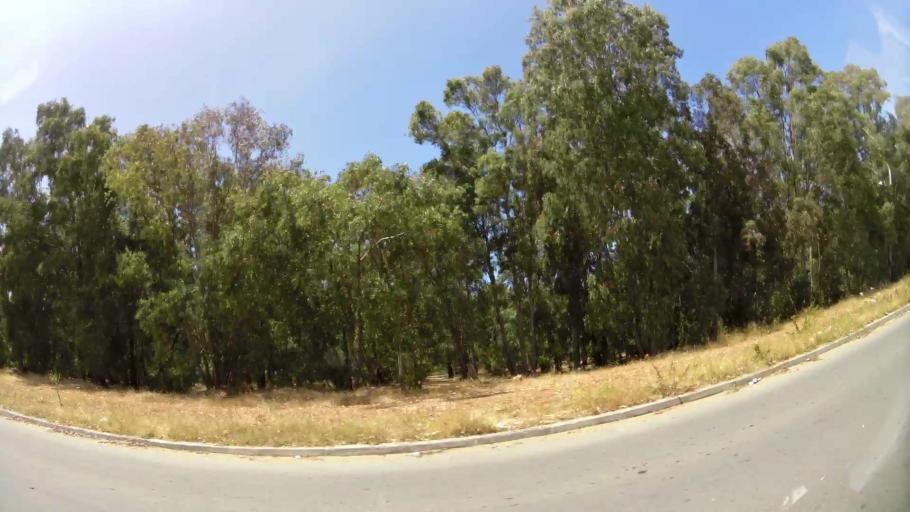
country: MA
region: Gharb-Chrarda-Beni Hssen
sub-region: Kenitra Province
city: Kenitra
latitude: 34.2679
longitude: -6.6320
